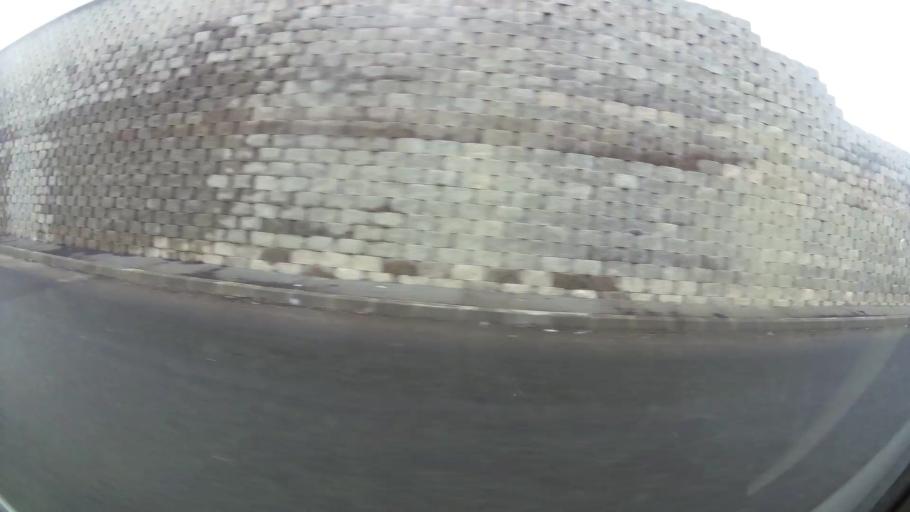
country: RO
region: Ilfov
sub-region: Comuna Popesti-Leordeni
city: Popesti-Leordeni
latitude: 44.3998
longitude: 26.1607
